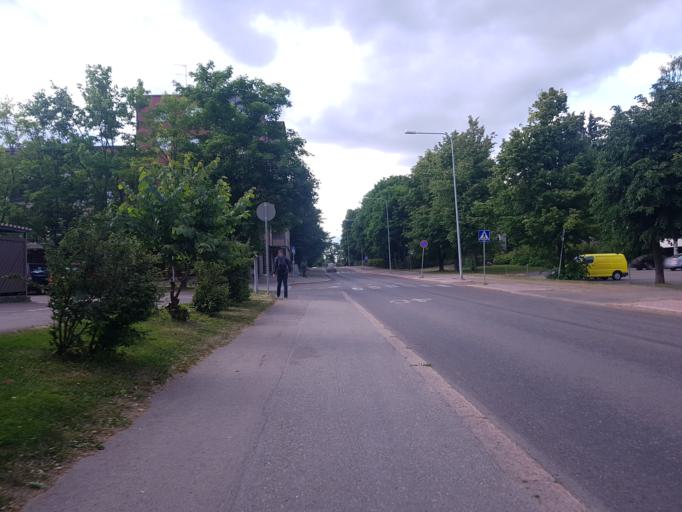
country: FI
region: Uusimaa
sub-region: Helsinki
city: Vantaa
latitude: 60.2456
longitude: 24.9927
